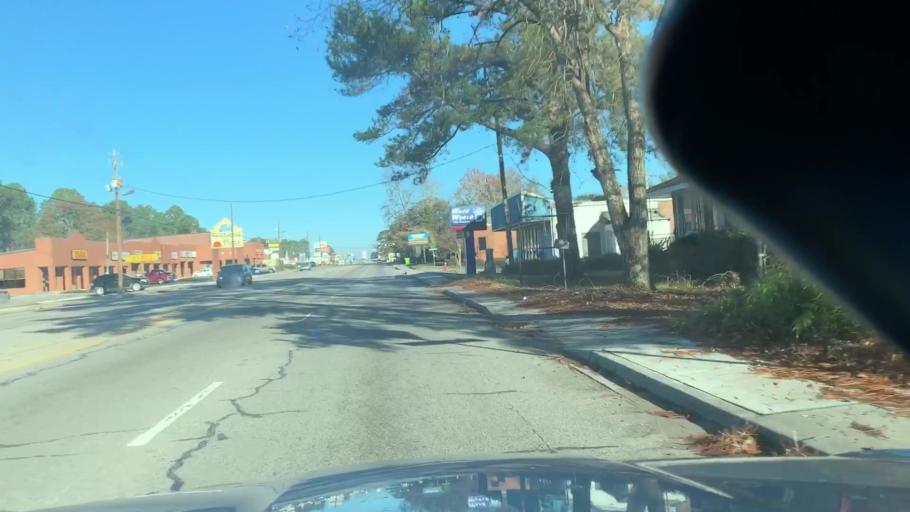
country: US
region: South Carolina
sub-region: Richland County
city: Woodfield
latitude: 34.0462
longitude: -80.9427
